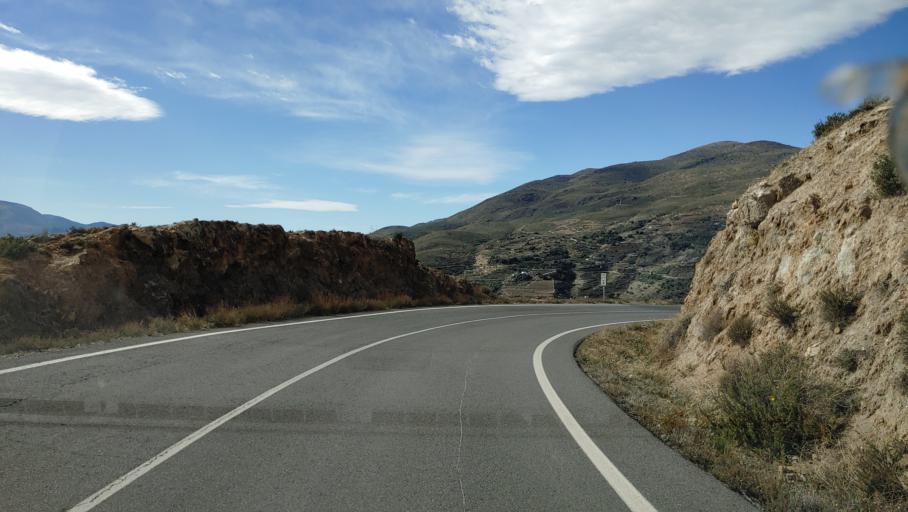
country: ES
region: Andalusia
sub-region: Provincia de Almeria
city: Ohanes
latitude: 37.0310
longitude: -2.7351
